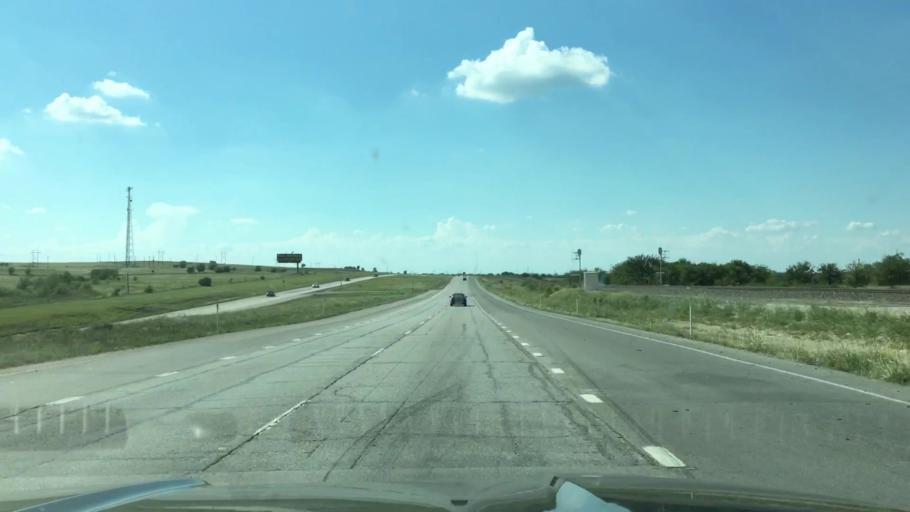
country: US
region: Texas
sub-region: Wise County
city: New Fairview
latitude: 33.1512
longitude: -97.5091
